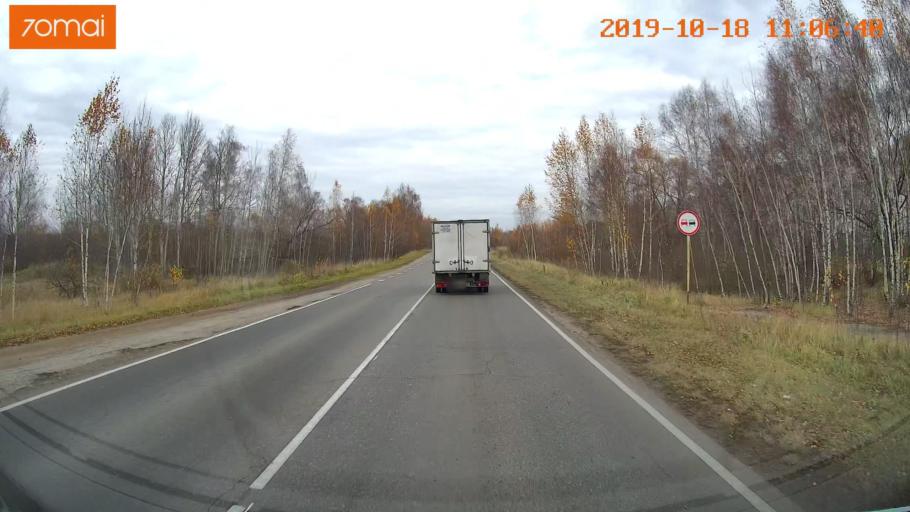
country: RU
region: Tula
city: Kimovsk
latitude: 53.9204
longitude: 38.5348
